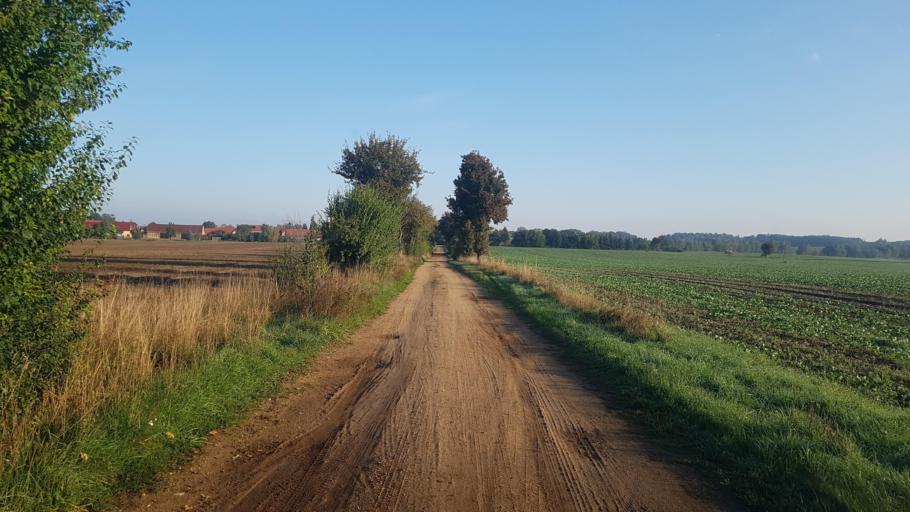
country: DE
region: Brandenburg
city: Lebusa
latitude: 51.8102
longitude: 13.4506
